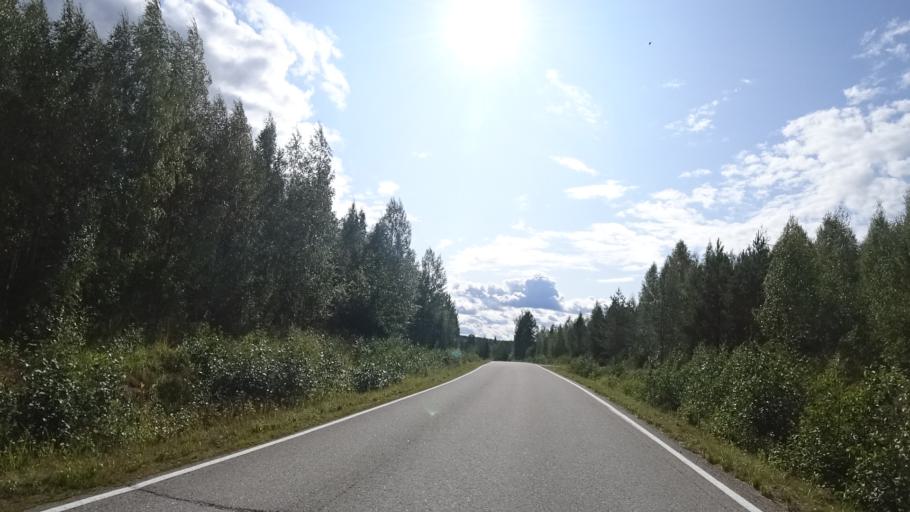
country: FI
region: North Karelia
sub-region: Joensuu
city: Ilomantsi
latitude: 62.4103
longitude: 30.9710
